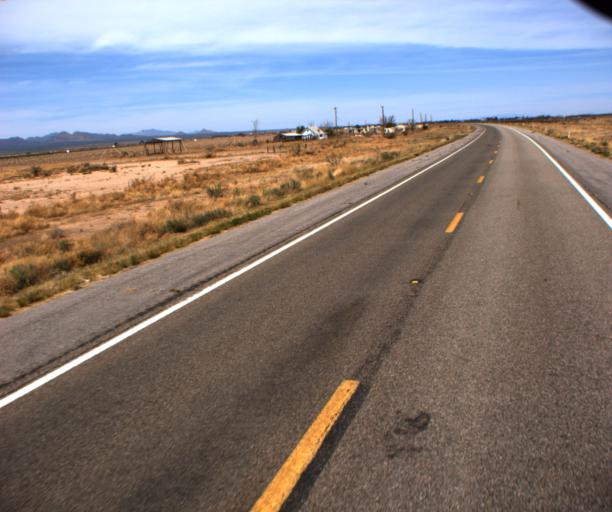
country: US
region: Arizona
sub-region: Cochise County
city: Pirtleville
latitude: 31.6475
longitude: -109.6730
